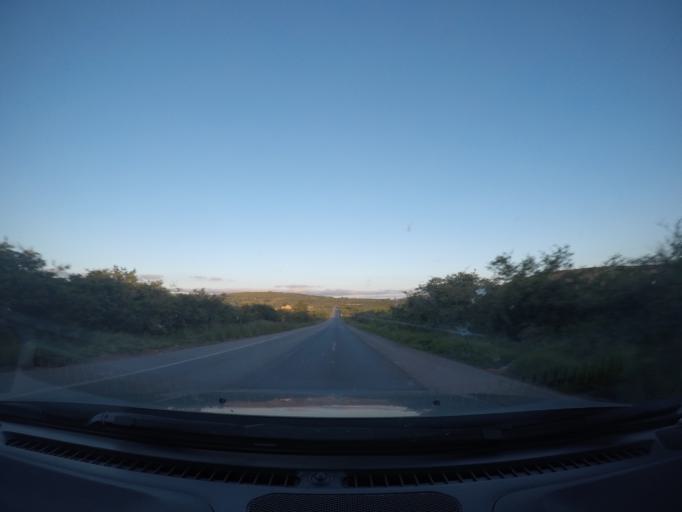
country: BR
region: Bahia
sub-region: Seabra
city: Seabra
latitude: -12.3903
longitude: -41.9015
